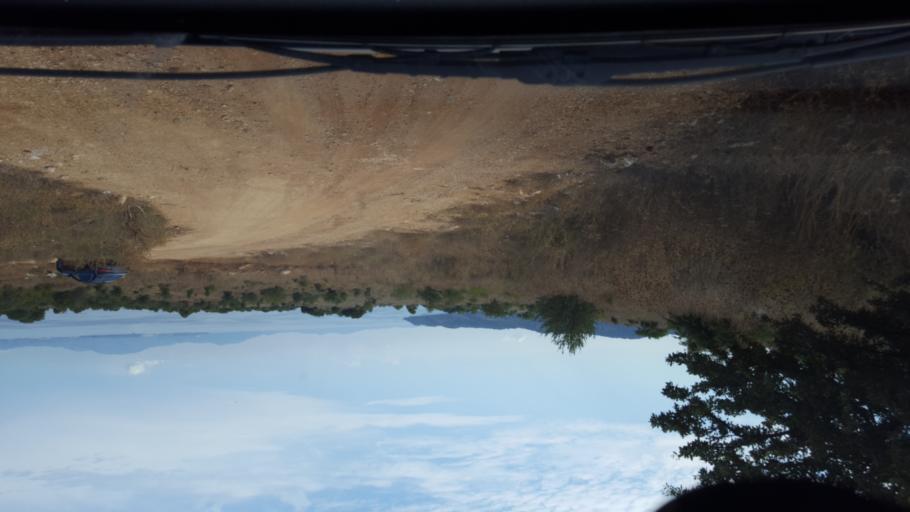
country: AL
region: Vlore
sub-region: Rrethi i Sarandes
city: Xarre
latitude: 39.7531
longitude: 19.9801
